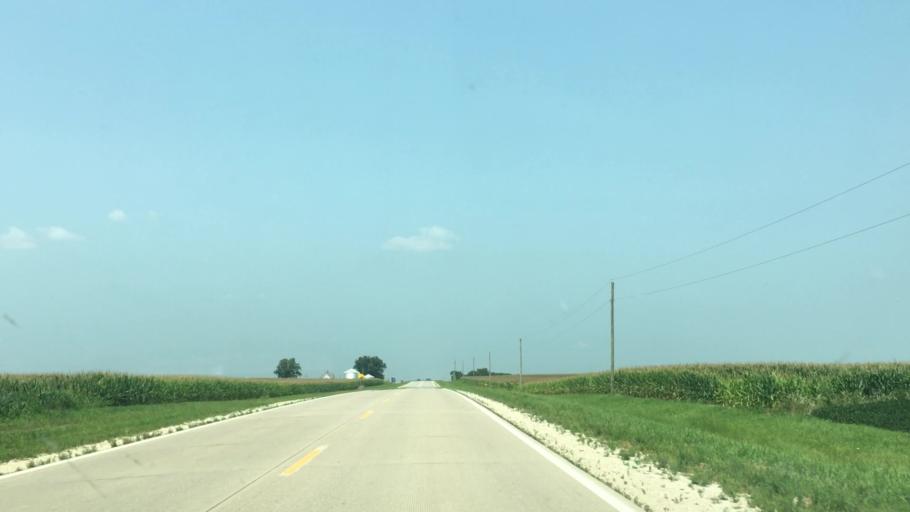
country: US
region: Iowa
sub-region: Fayette County
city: Oelwein
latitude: 42.7127
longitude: -91.8047
